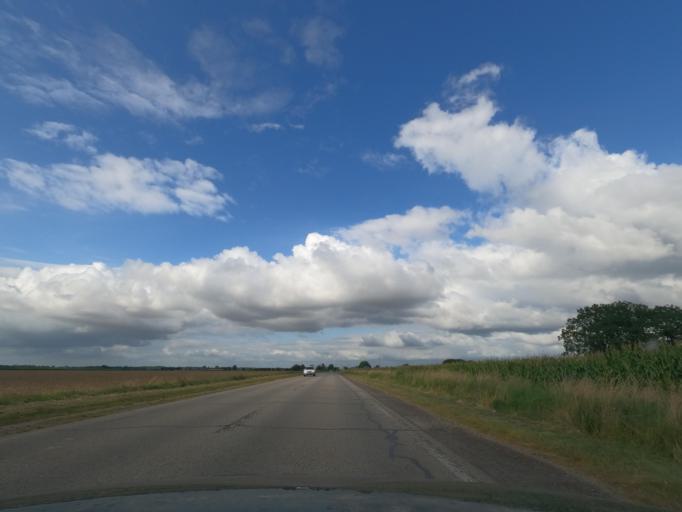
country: FR
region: Haute-Normandie
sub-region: Departement de l'Eure
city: Broglie
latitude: 49.0092
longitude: 0.5155
